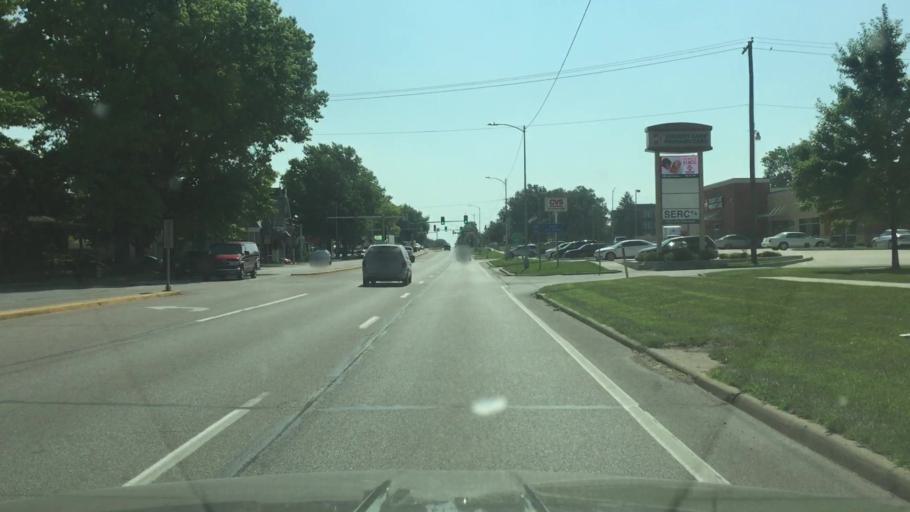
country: US
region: Missouri
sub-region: Pettis County
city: Sedalia
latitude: 38.7042
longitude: -93.2298
